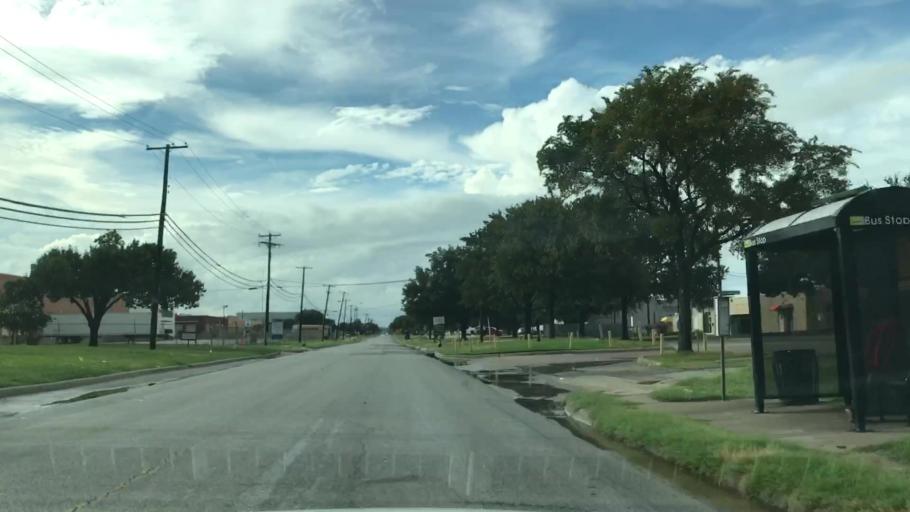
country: US
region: Texas
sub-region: Dallas County
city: Dallas
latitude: 32.8158
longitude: -96.8737
